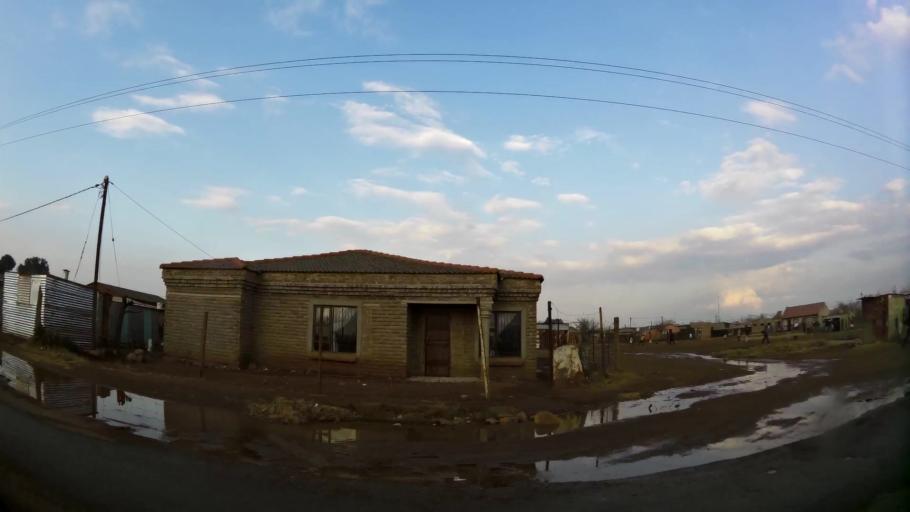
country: ZA
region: Gauteng
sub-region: City of Johannesburg Metropolitan Municipality
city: Orange Farm
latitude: -26.5492
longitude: 27.8331
